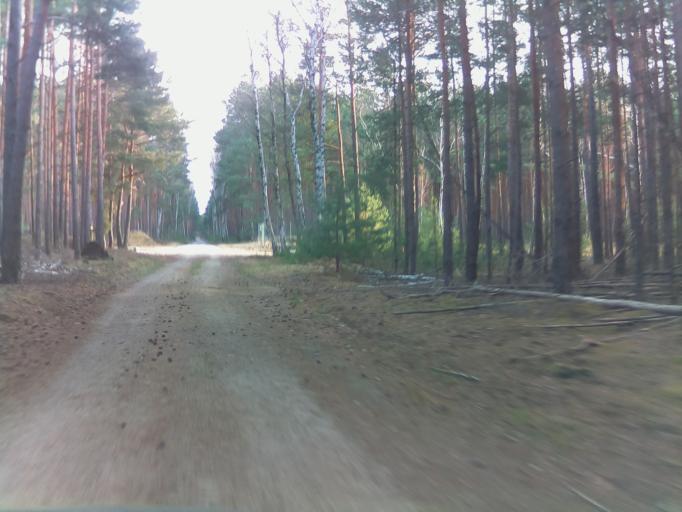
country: DE
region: Brandenburg
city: Tauer
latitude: 51.9897
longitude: 14.4690
